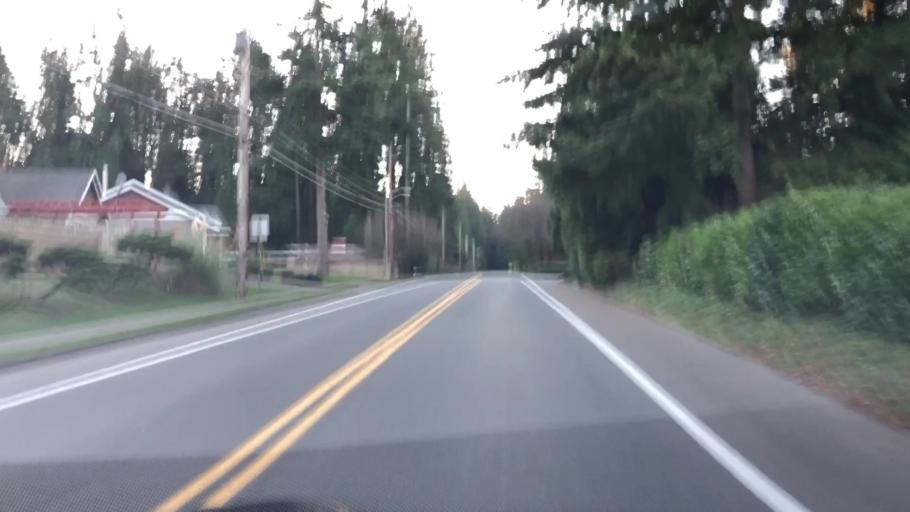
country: US
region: Washington
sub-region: King County
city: Kirkland
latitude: 47.6647
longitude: -122.1775
